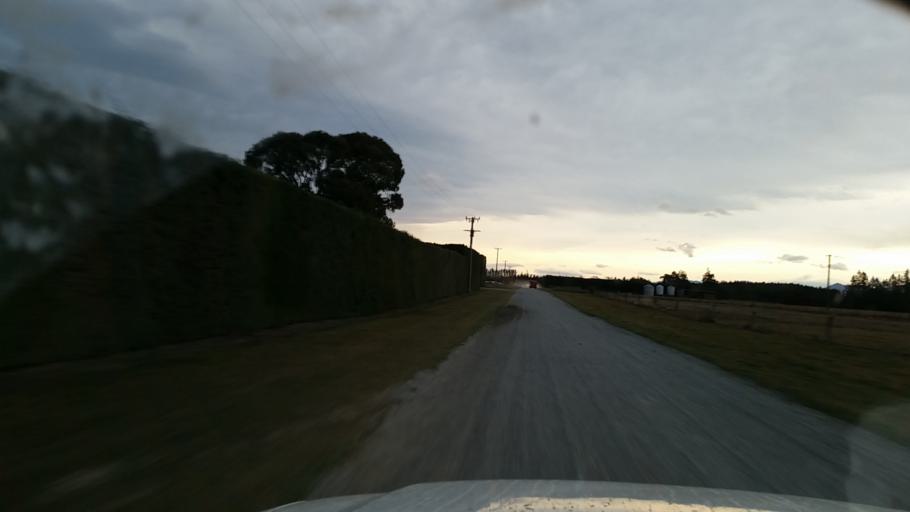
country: NZ
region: Canterbury
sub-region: Ashburton District
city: Tinwald
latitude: -43.8344
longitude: 171.6195
